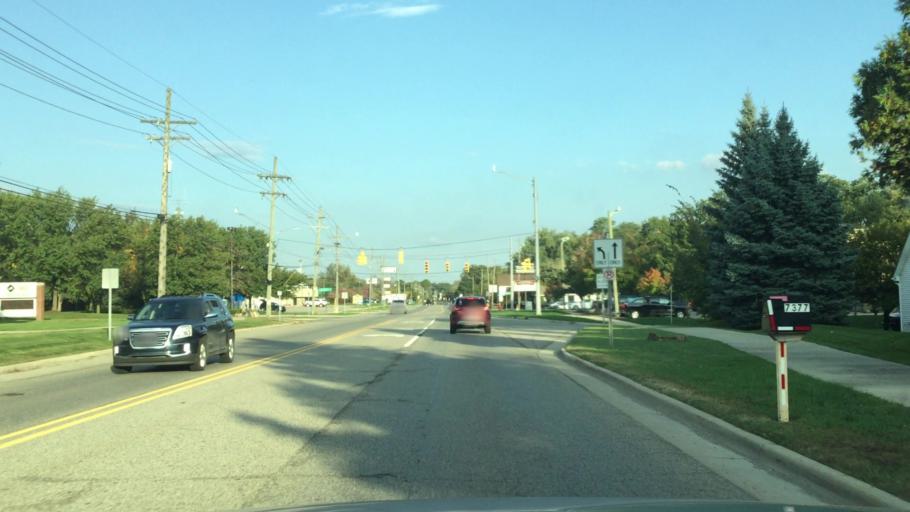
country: US
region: Michigan
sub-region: Oakland County
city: West Bloomfield Township
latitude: 42.6152
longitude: -83.4302
